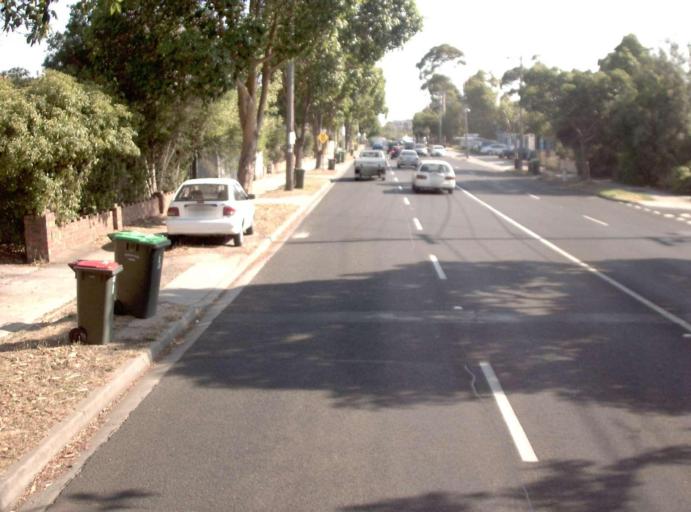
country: AU
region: Victoria
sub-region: Whitehorse
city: Box Hill South
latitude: -37.8273
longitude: 145.1221
